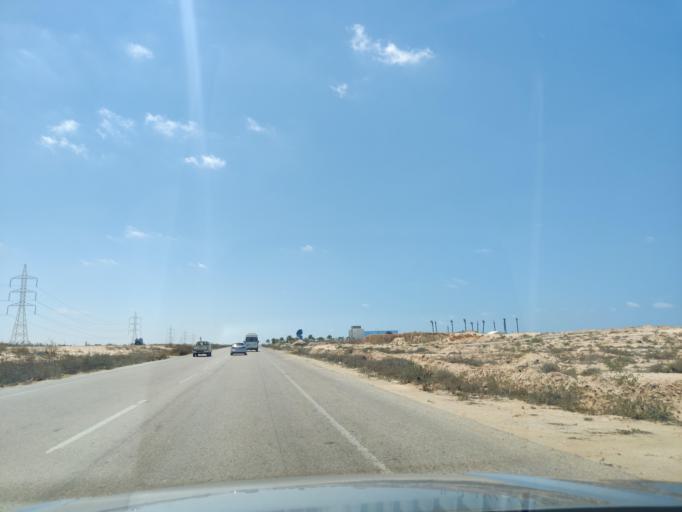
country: EG
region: Muhafazat Matruh
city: Al `Alamayn
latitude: 31.0679
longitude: 28.1720
